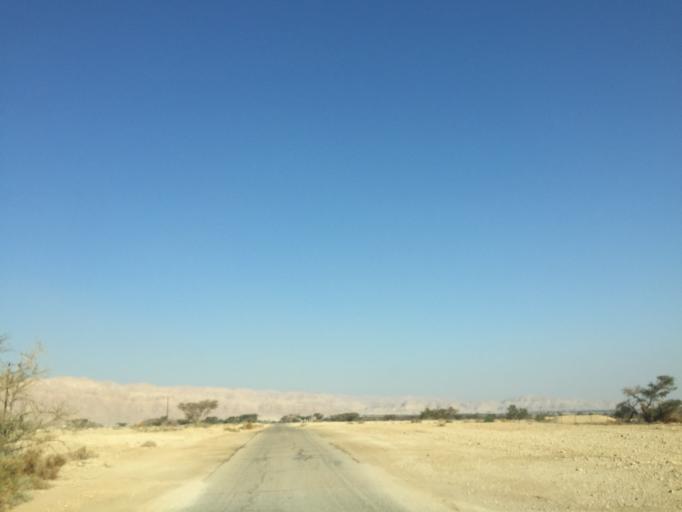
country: JO
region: Ma'an
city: Al Quwayrah
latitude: 29.8363
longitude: 35.0316
